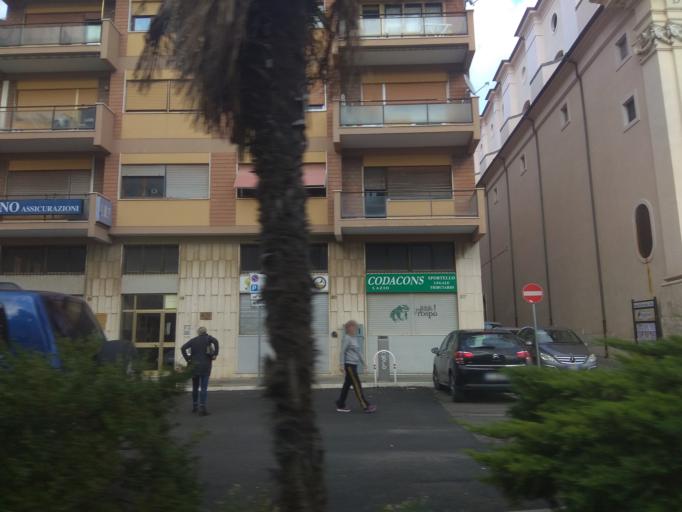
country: IT
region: Latium
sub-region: Citta metropolitana di Roma Capitale
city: Civitavecchia
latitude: 42.0925
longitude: 11.7917
